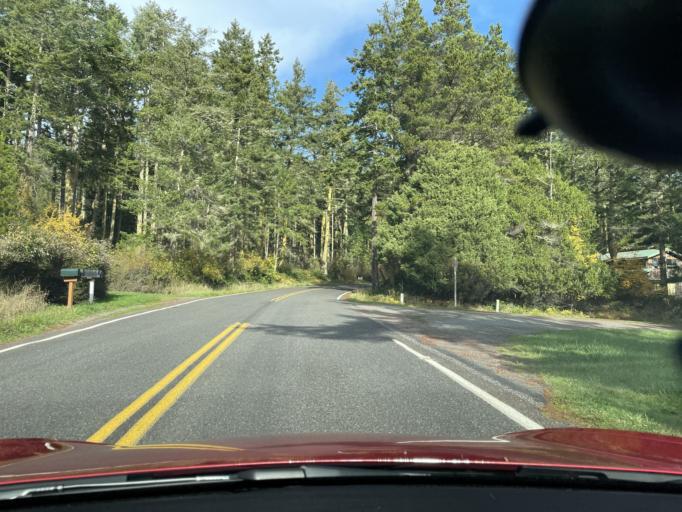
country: US
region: Washington
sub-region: San Juan County
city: Friday Harbor
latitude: 48.5215
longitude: -122.9755
